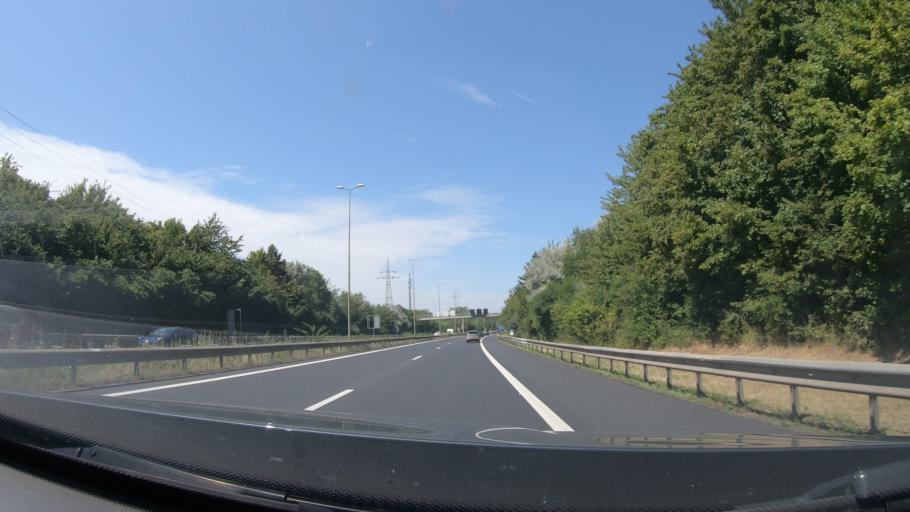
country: LU
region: Luxembourg
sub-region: Canton de Luxembourg
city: Hesperange
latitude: 49.5750
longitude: 6.1387
